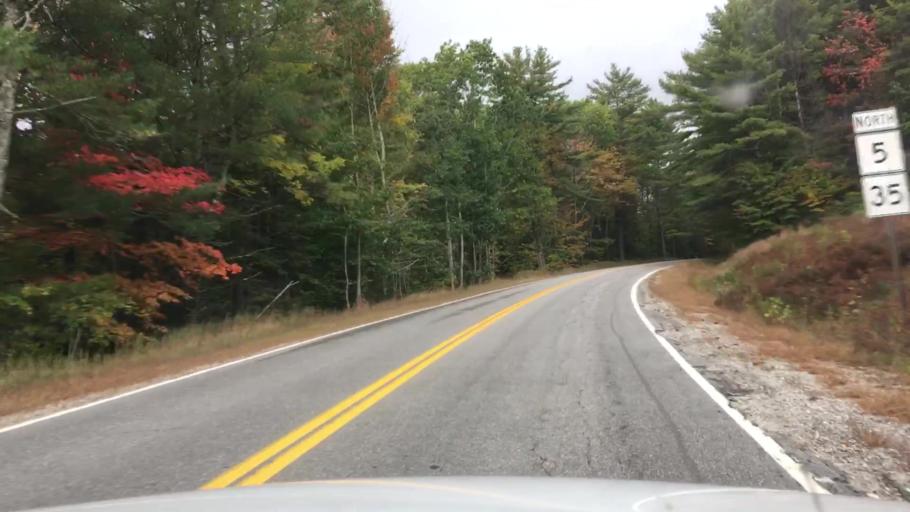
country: US
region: Maine
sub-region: Oxford County
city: Bethel
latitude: 44.3400
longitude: -70.7831
